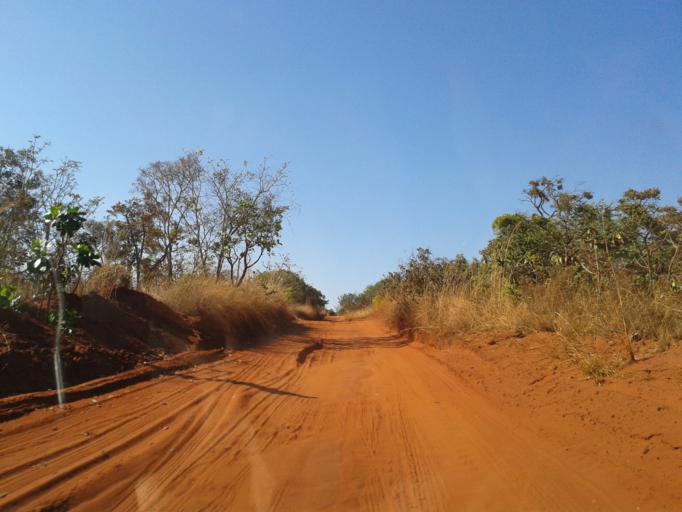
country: BR
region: Minas Gerais
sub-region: Ituiutaba
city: Ituiutaba
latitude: -19.0132
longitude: -49.3608
